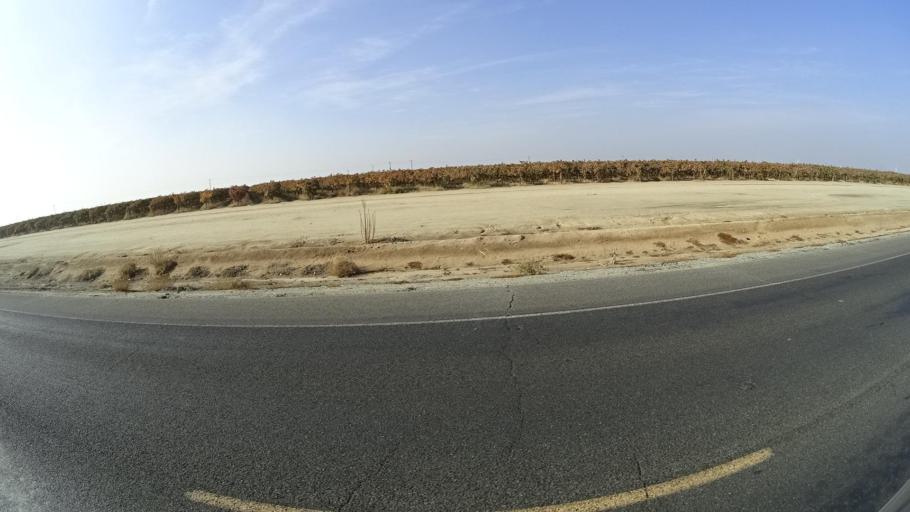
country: US
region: California
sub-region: Tulare County
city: Richgrove
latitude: 35.7641
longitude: -119.1311
